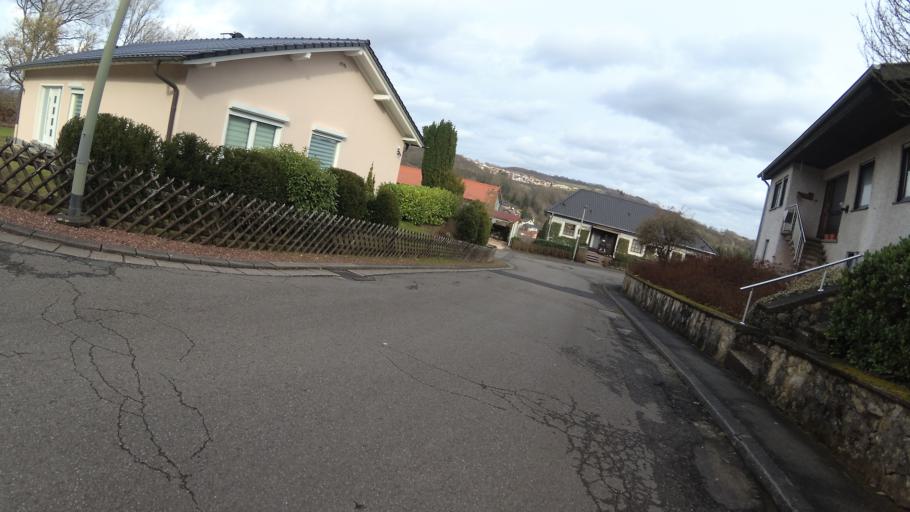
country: DE
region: Saarland
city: Ottweiler
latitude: 49.3938
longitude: 7.1666
